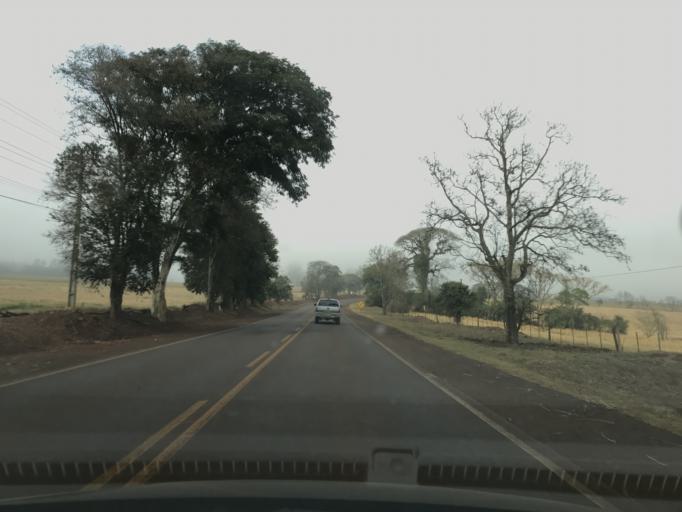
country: BR
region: Parana
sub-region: Toledo
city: Toledo
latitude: -24.7030
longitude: -53.6980
